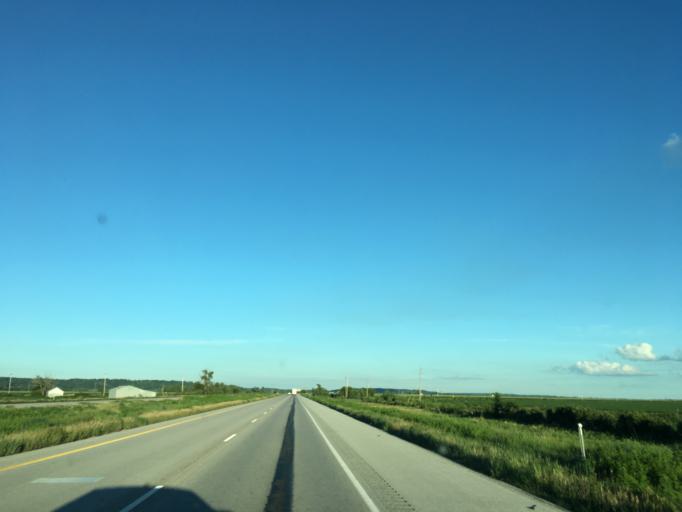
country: US
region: Iowa
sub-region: Fremont County
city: Hamburg
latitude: 40.6317
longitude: -95.7211
